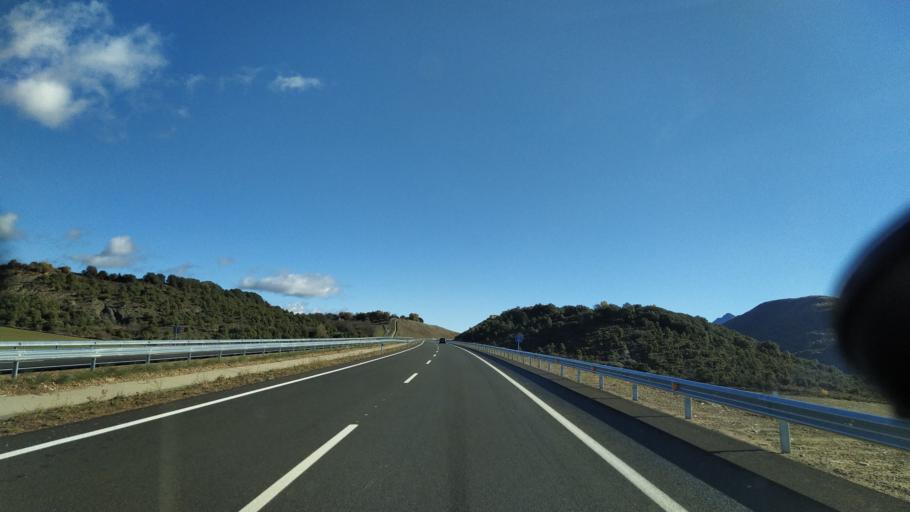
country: ES
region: Aragon
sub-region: Provincia de Huesca
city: Santa Cruz de la Seros
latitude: 42.5634
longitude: -0.6894
